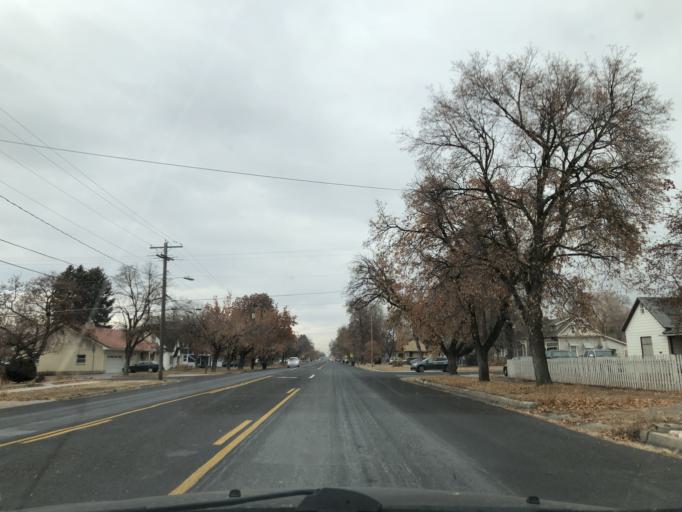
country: US
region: Utah
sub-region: Cache County
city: Logan
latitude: 41.7217
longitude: -111.8378
